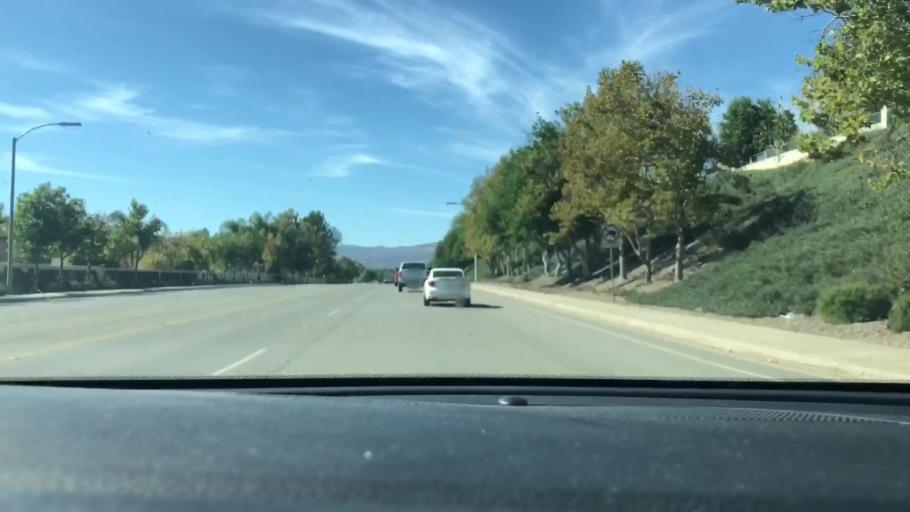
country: US
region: California
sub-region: Riverside County
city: Murrieta
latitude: 33.5957
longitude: -117.1983
